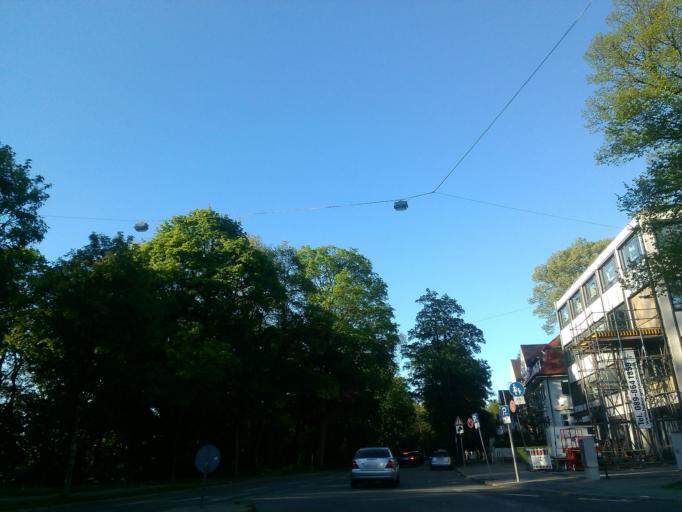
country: DE
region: Bavaria
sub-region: Upper Bavaria
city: Bogenhausen
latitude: 48.1510
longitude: 11.6084
